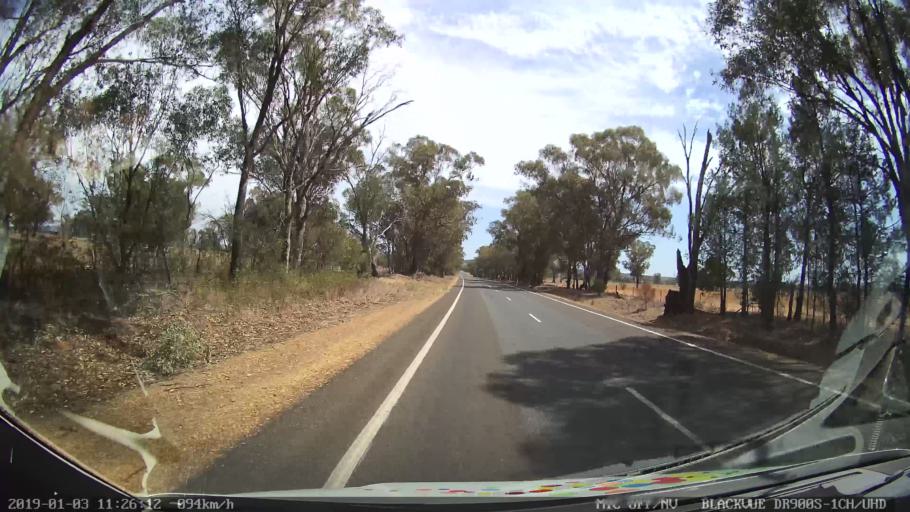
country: AU
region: New South Wales
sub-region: Weddin
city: Grenfell
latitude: -34.0281
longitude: 148.2265
